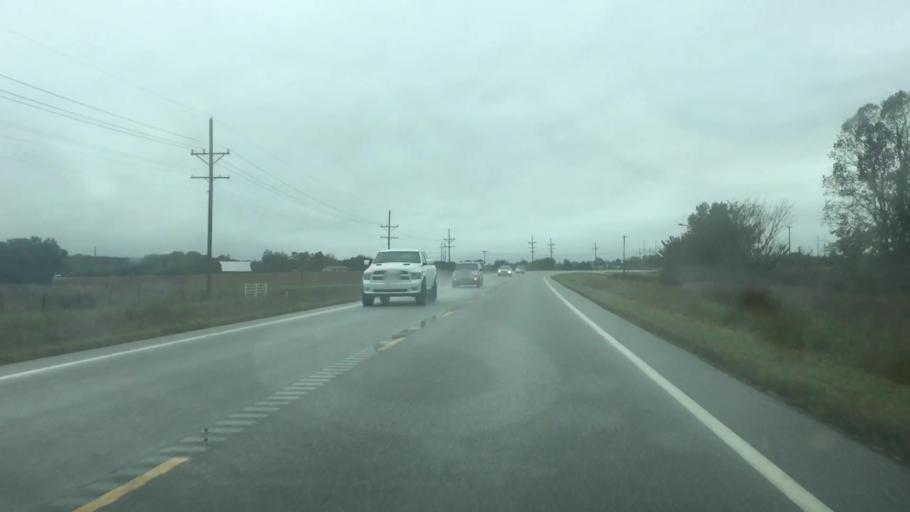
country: US
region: Kansas
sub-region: Anderson County
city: Garnett
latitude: 38.3398
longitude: -95.1651
